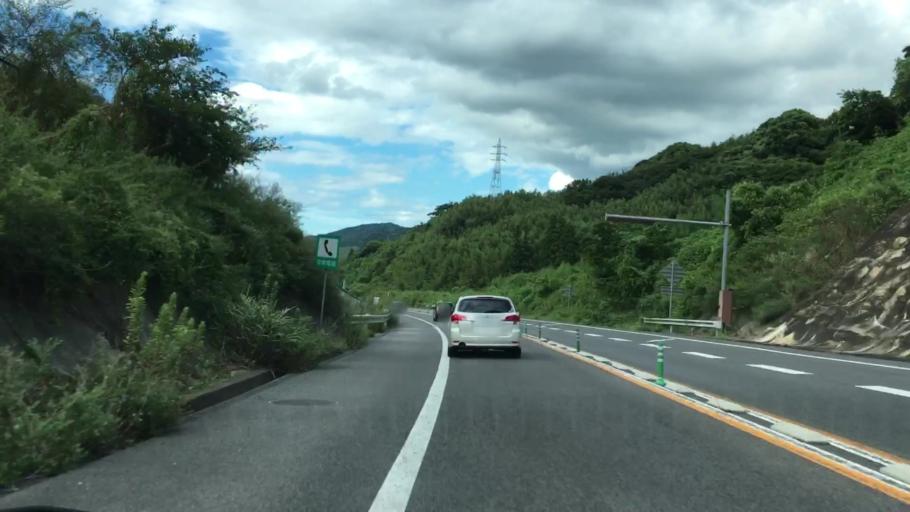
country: JP
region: Saga Prefecture
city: Karatsu
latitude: 33.4316
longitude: 130.0483
